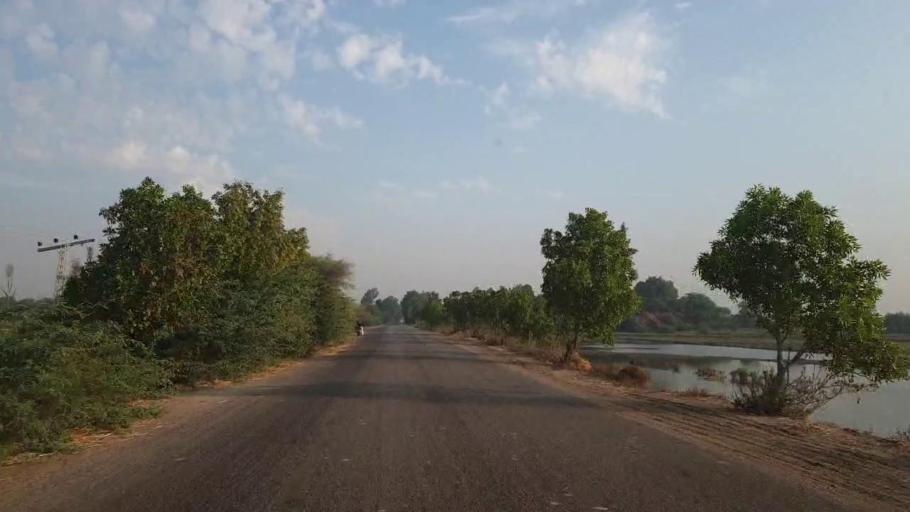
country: PK
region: Sindh
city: Tando Bago
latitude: 24.7393
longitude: 68.9465
